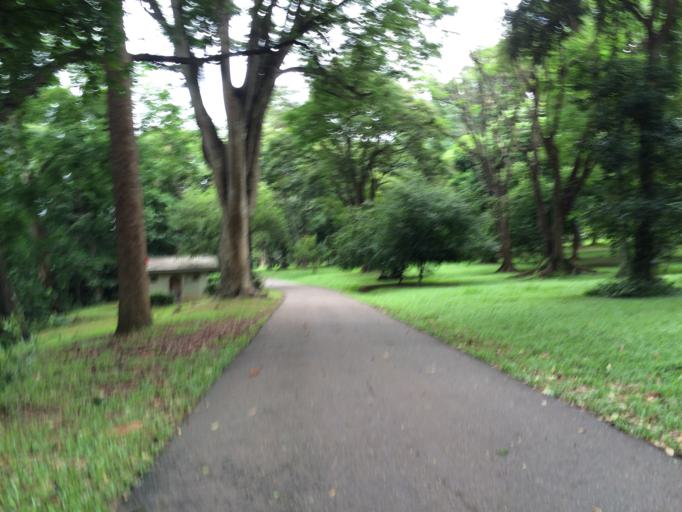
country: LK
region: Central
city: Kandy
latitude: 7.2729
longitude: 80.5935
